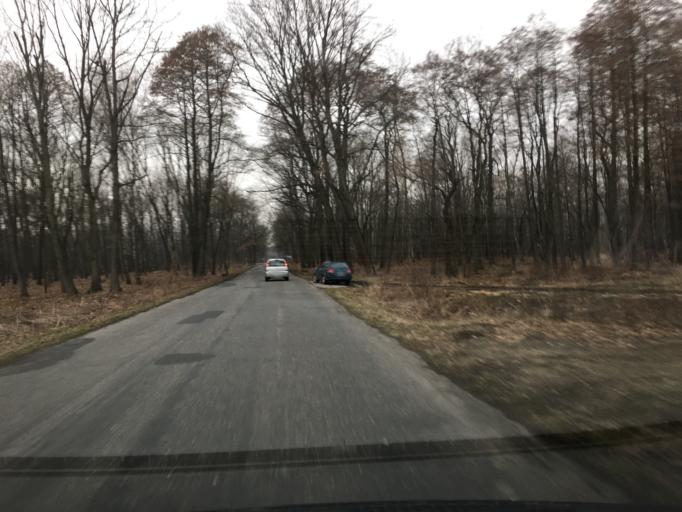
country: PL
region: Opole Voivodeship
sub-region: Powiat kedzierzynsko-kozielski
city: Kedzierzyn-Kozle
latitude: 50.3209
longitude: 18.2376
